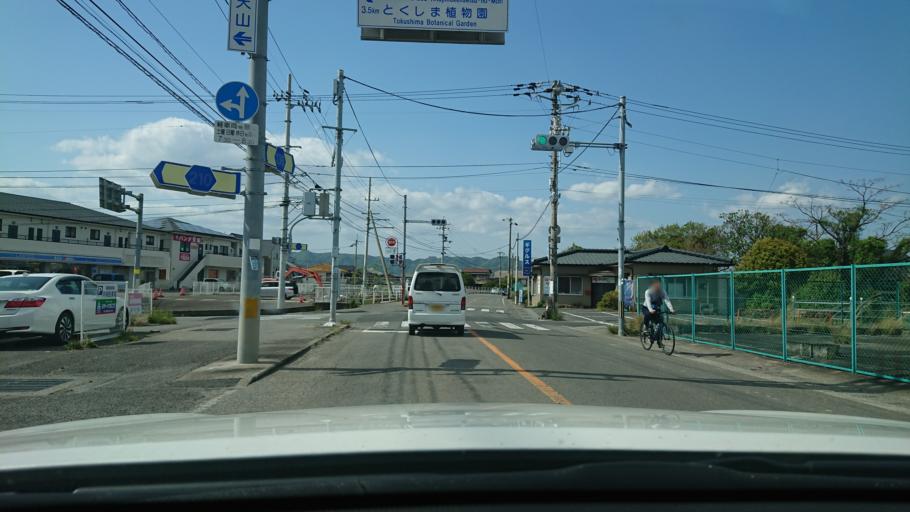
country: JP
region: Tokushima
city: Komatsushimacho
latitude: 34.0227
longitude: 134.5508
